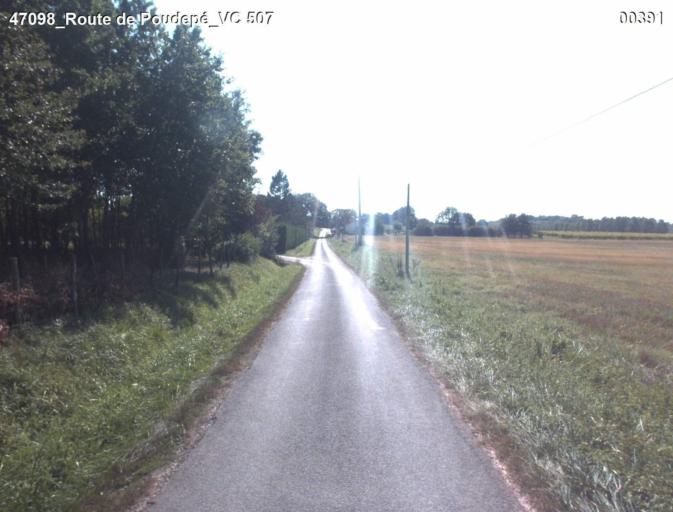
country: FR
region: Aquitaine
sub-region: Departement du Lot-et-Garonne
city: Nerac
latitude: 44.1108
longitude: 0.4147
